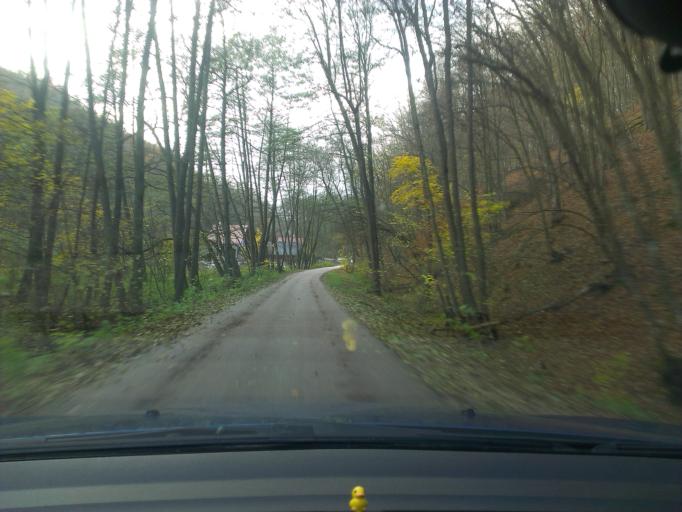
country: SK
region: Trnavsky
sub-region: Okres Trnava
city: Piestany
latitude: 48.6080
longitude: 17.9235
